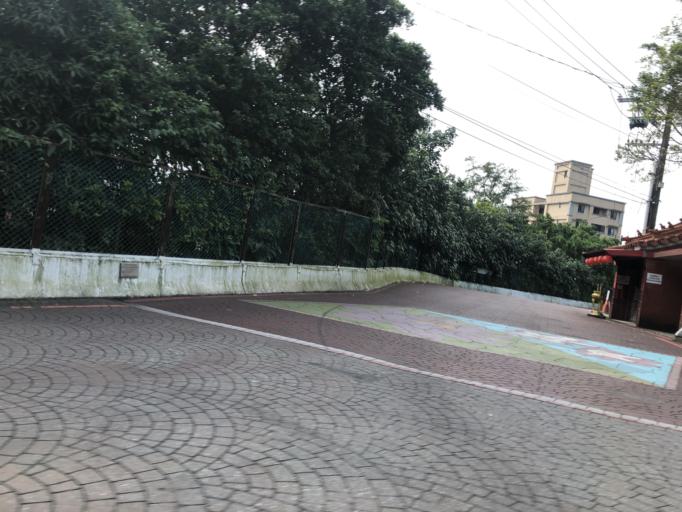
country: TW
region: Taiwan
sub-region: Keelung
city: Keelung
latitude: 25.2235
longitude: 121.6373
